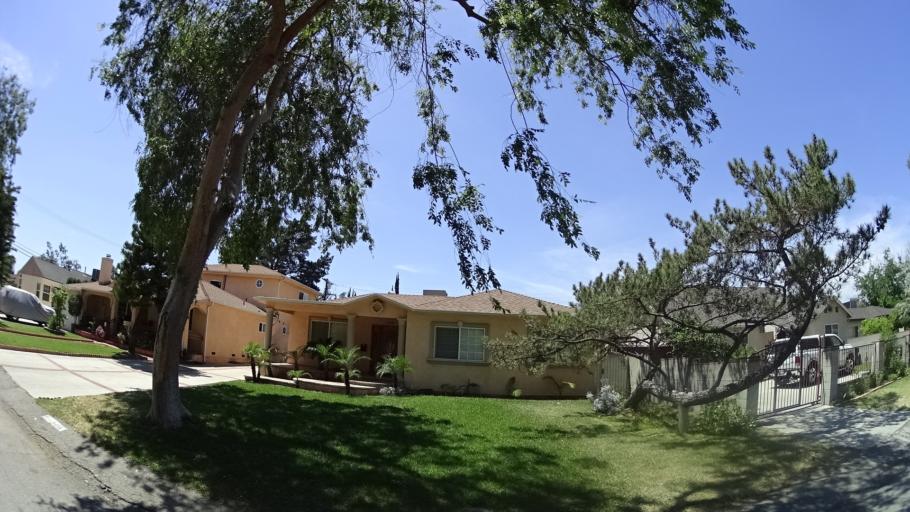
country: US
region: California
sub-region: Los Angeles County
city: North Hollywood
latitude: 34.1836
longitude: -118.3769
